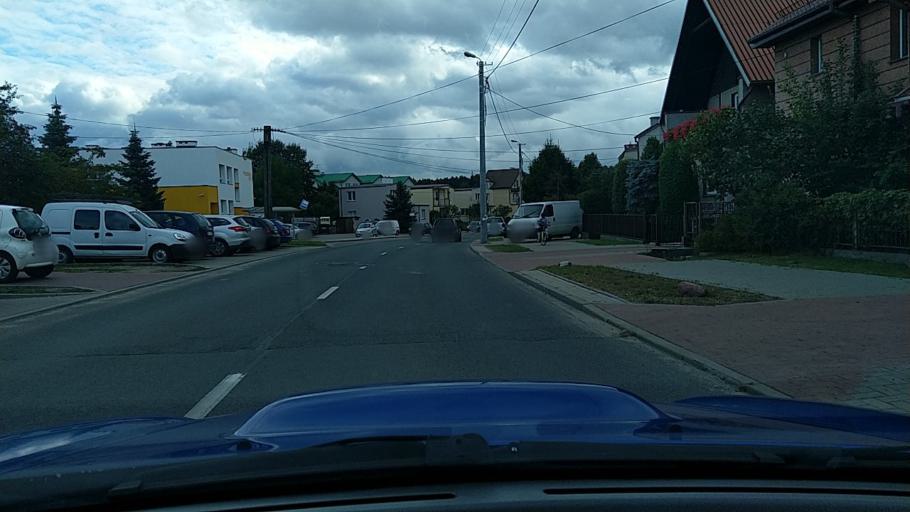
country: PL
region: Warmian-Masurian Voivodeship
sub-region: Olsztyn
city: Kortowo
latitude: 53.7653
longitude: 20.4279
